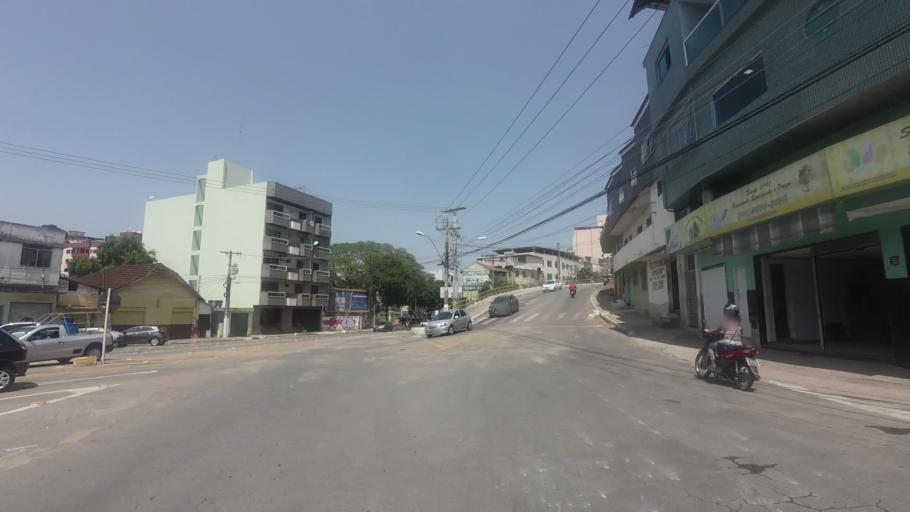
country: BR
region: Espirito Santo
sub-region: Cachoeiro De Itapemirim
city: Cachoeiro de Itapemirim
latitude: -20.8399
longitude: -41.1228
